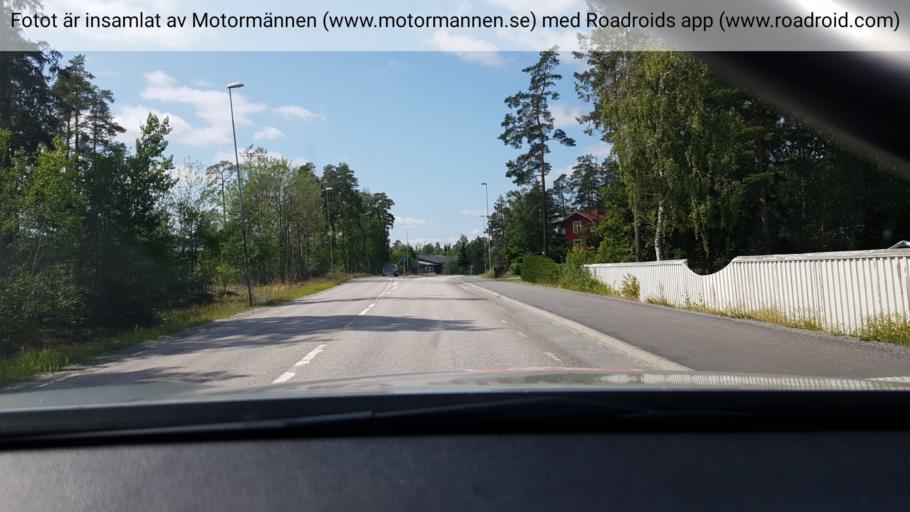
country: SE
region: Stockholm
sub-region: Vallentuna Kommun
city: Vallentuna
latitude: 59.5309
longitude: 18.1112
